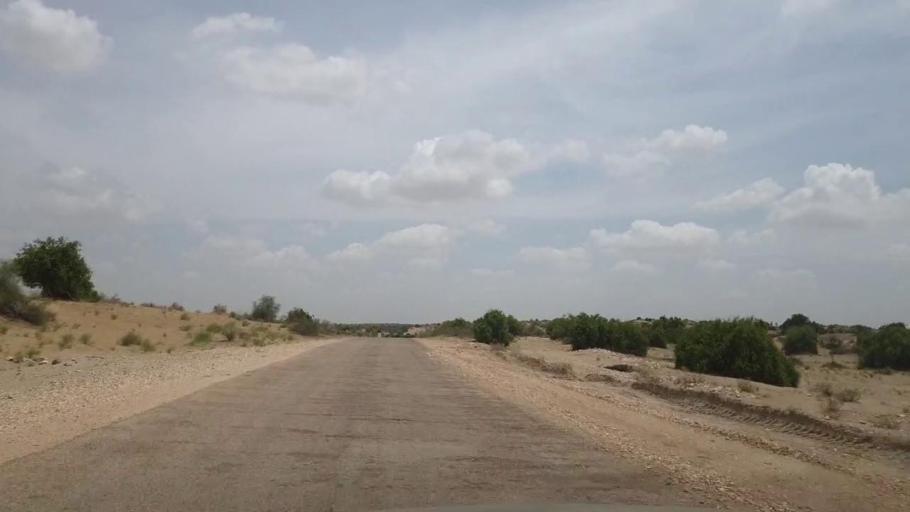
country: PK
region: Sindh
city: Kot Diji
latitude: 27.1863
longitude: 69.1707
